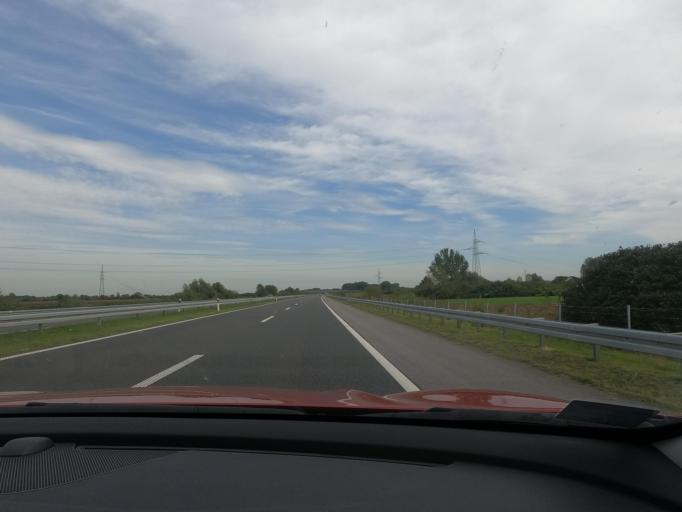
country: HR
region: Brodsko-Posavska
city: Sikirevci
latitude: 45.1224
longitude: 18.4629
